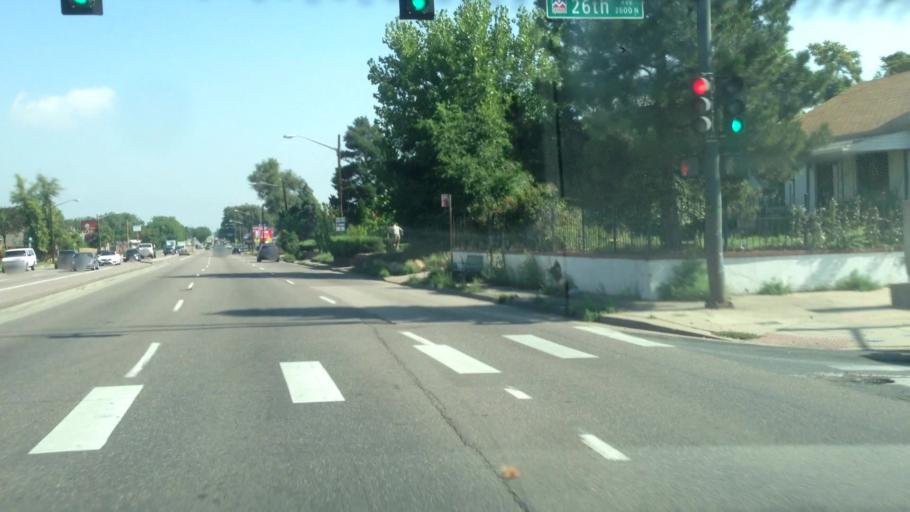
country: US
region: Colorado
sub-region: Denver County
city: Denver
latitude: 39.7546
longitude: -104.9406
